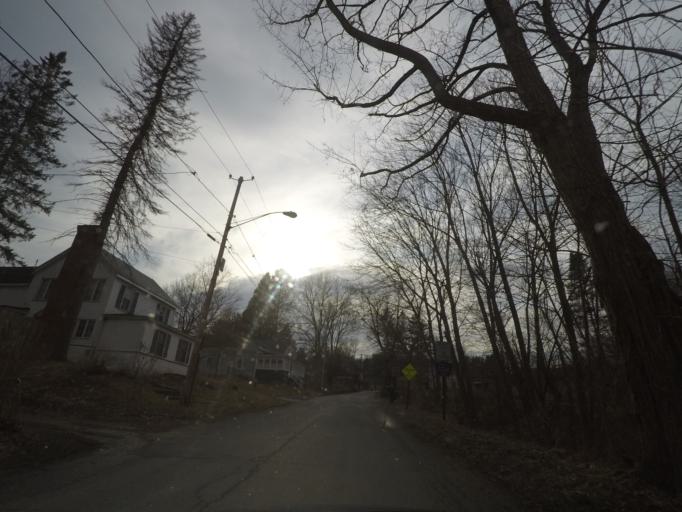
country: US
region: New York
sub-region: Rensselaer County
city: Hoosick Falls
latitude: 42.9082
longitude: -73.3618
